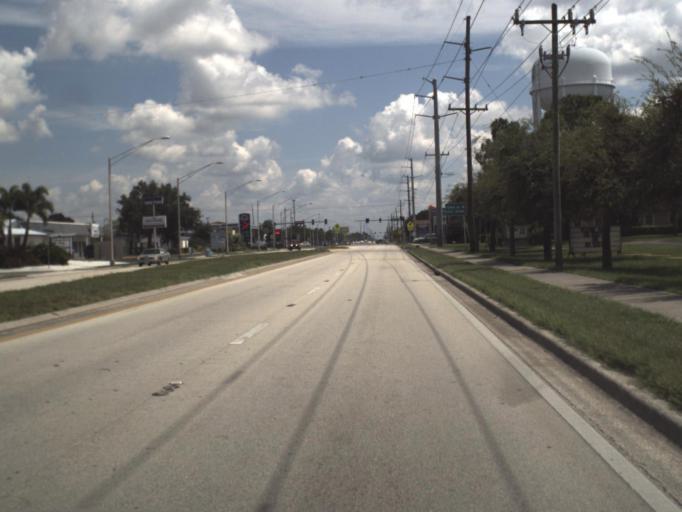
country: US
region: Florida
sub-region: Manatee County
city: West Bradenton
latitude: 27.4625
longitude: -82.6233
